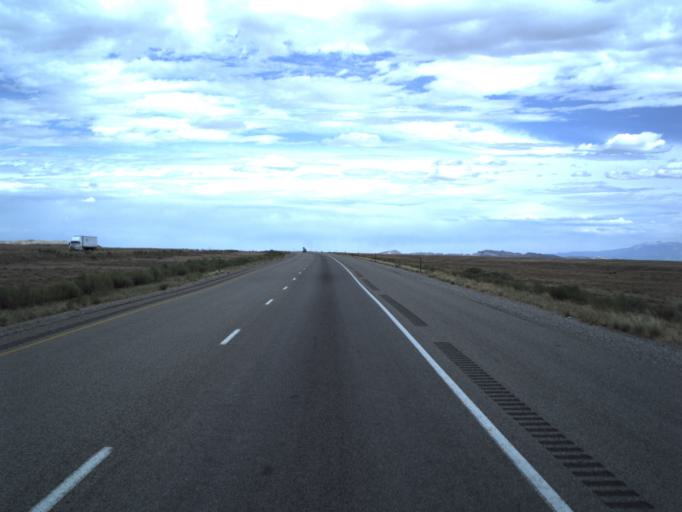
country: US
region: Utah
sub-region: Grand County
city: Moab
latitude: 38.9232
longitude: -109.9740
